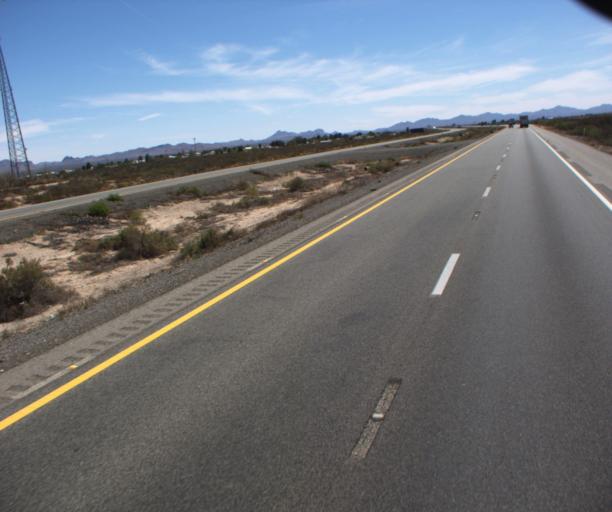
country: US
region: New Mexico
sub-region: Hidalgo County
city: Lordsburg
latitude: 32.2669
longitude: -109.2392
